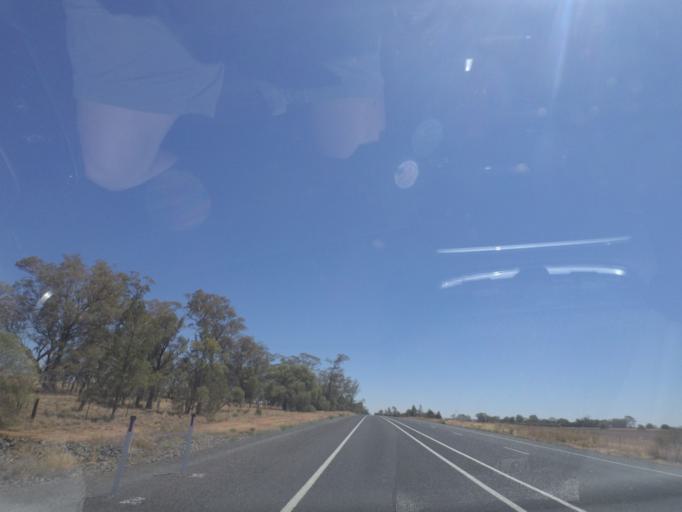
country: AU
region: New South Wales
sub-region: Gilgandra
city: Gilgandra
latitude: -31.4939
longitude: 148.8671
